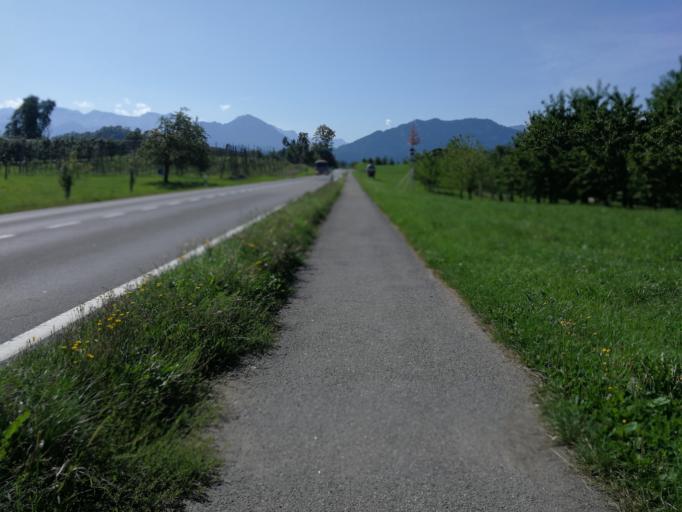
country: CH
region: Lucerne
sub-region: Lucerne-Land District
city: Weggis
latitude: 47.0491
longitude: 8.4262
